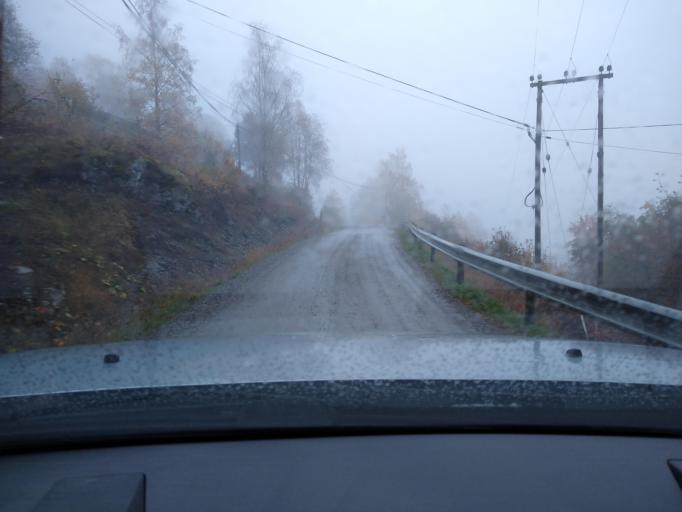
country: NO
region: Oppland
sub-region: Ringebu
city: Ringebu
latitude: 61.5265
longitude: 10.1608
